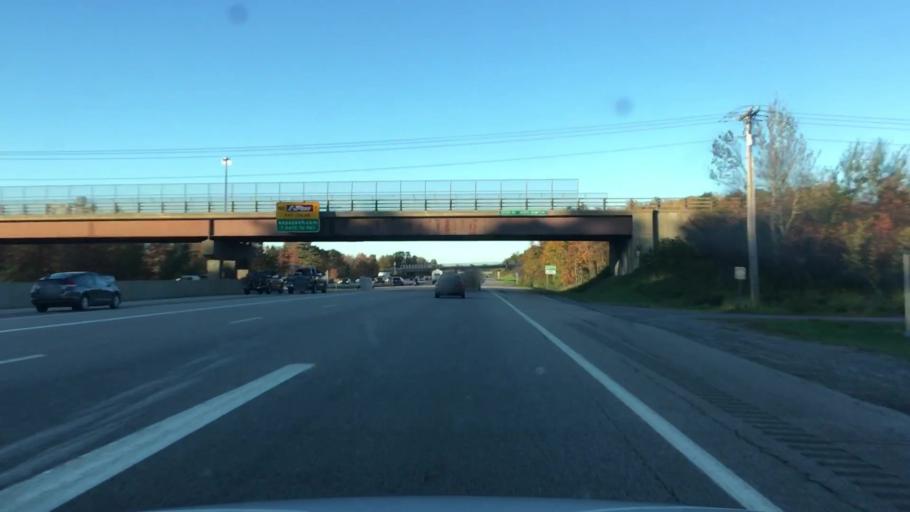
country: US
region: New Hampshire
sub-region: Rockingham County
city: North Hampton
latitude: 42.9685
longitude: -70.8548
